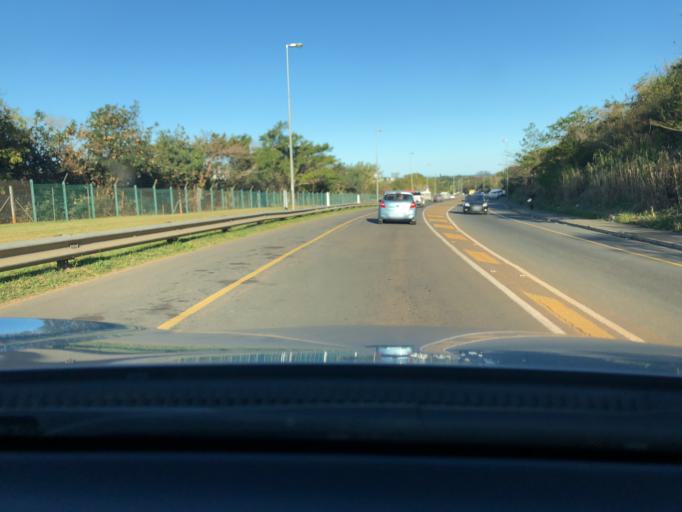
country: ZA
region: KwaZulu-Natal
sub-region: eThekwini Metropolitan Municipality
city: Umkomaas
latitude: -30.0288
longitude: 30.8848
